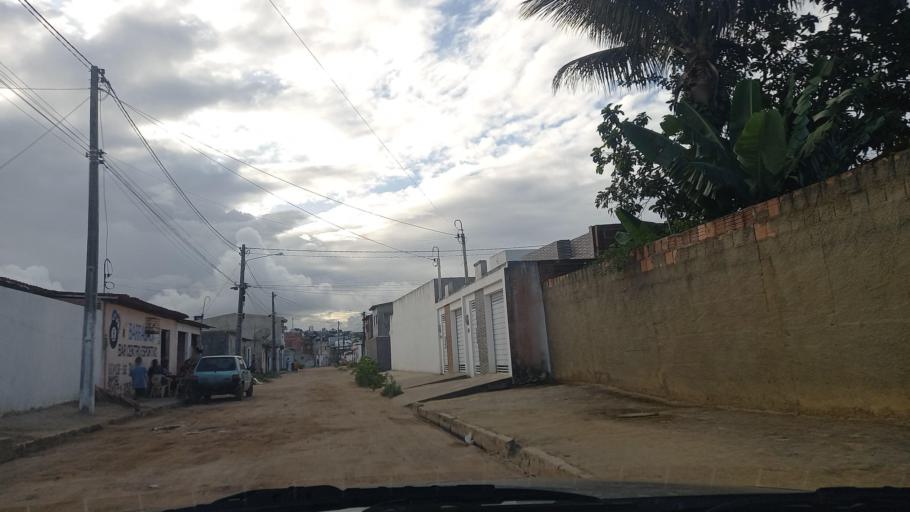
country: BR
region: Pernambuco
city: Garanhuns
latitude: -8.9150
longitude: -36.4821
